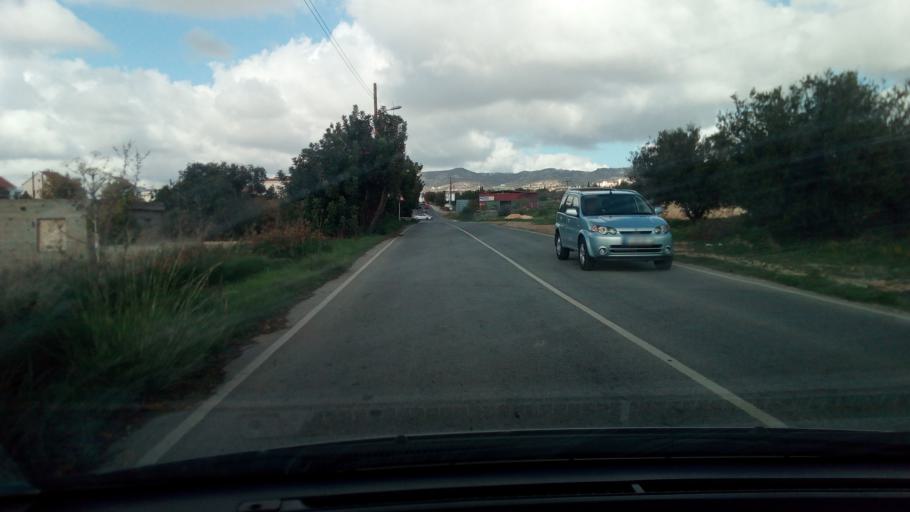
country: CY
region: Pafos
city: Mesogi
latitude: 34.8004
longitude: 32.4493
